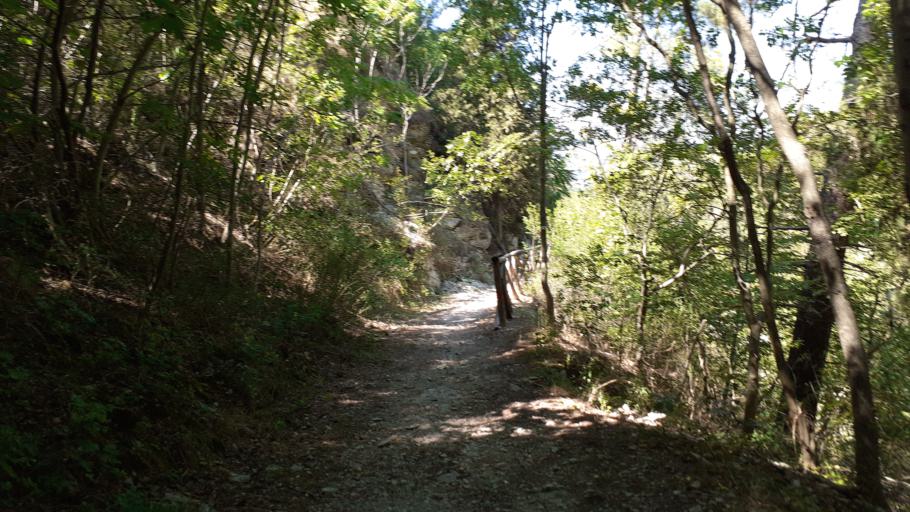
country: IT
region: Abruzzo
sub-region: Provincia di Pescara
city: San Valentino in Abruzzo Citeriore
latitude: 42.2437
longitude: 13.9667
